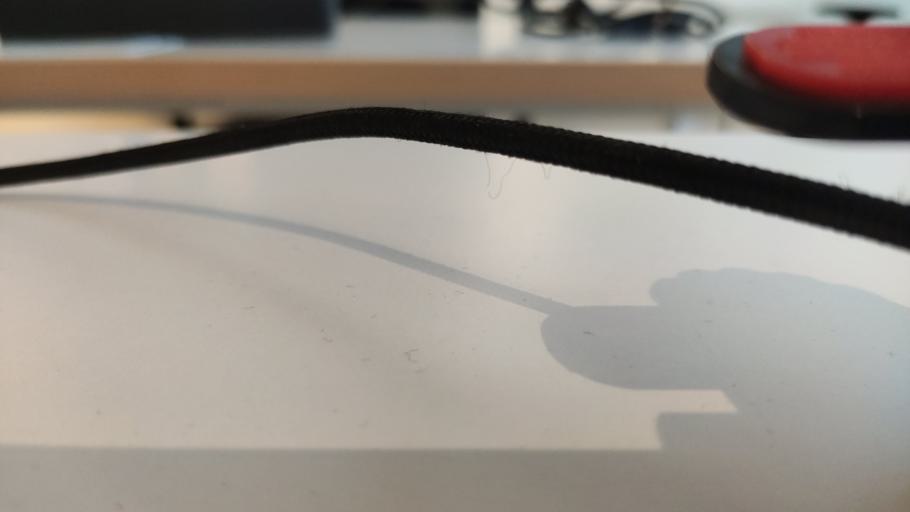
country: RU
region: Moskovskaya
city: Novopetrovskoye
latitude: 55.9536
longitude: 36.4382
